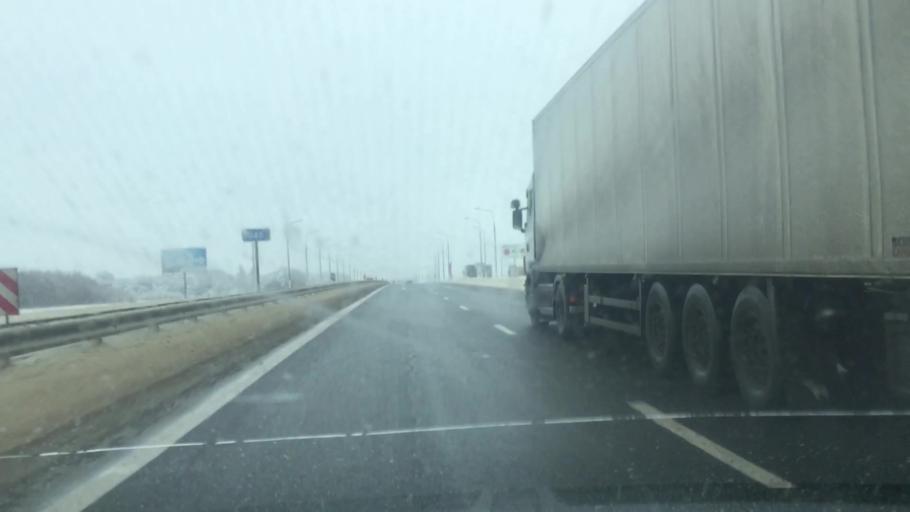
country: RU
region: Lipetsk
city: Stanovoye
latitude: 52.8903
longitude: 38.2422
